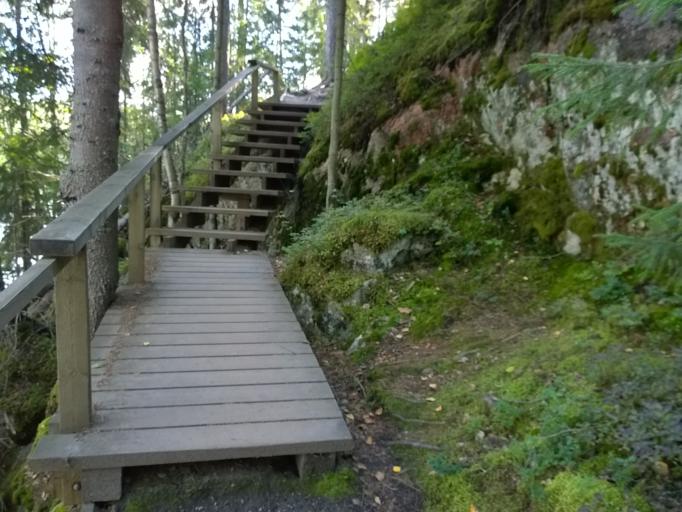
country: FI
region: Pirkanmaa
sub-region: Tampere
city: Tampere
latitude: 61.4399
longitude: 23.8286
